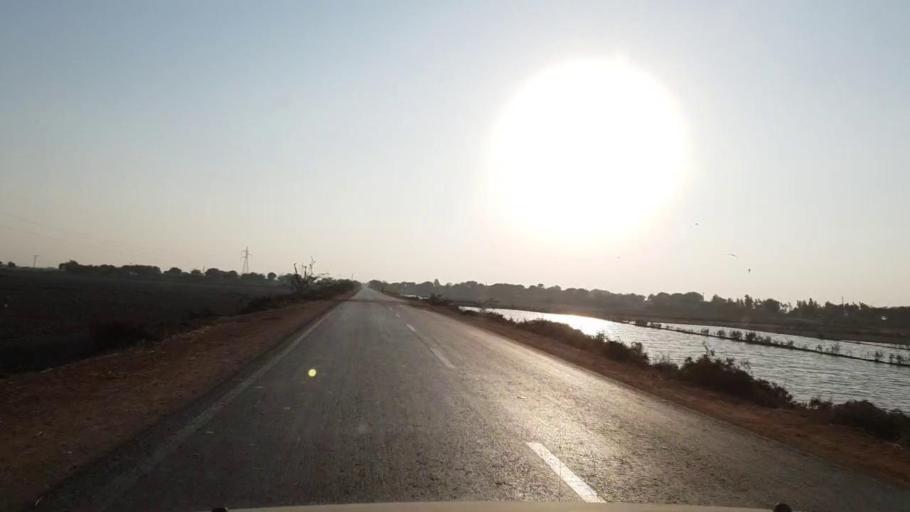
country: PK
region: Sindh
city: Daro Mehar
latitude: 24.6494
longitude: 68.1250
